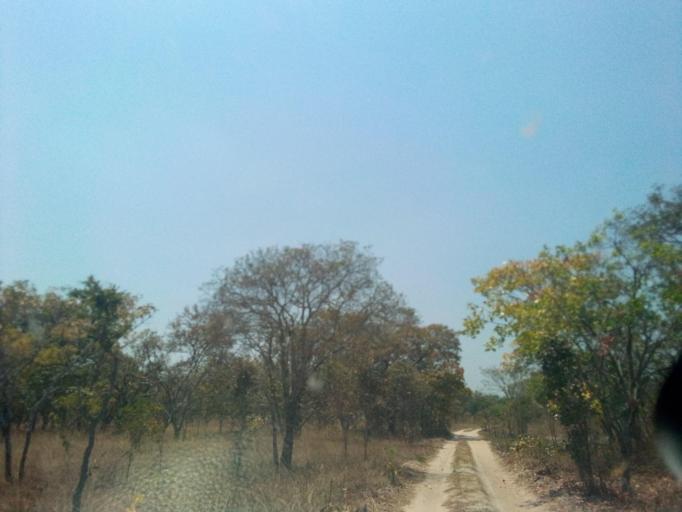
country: ZM
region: Copperbelt
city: Kataba
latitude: -12.2353
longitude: 30.4075
